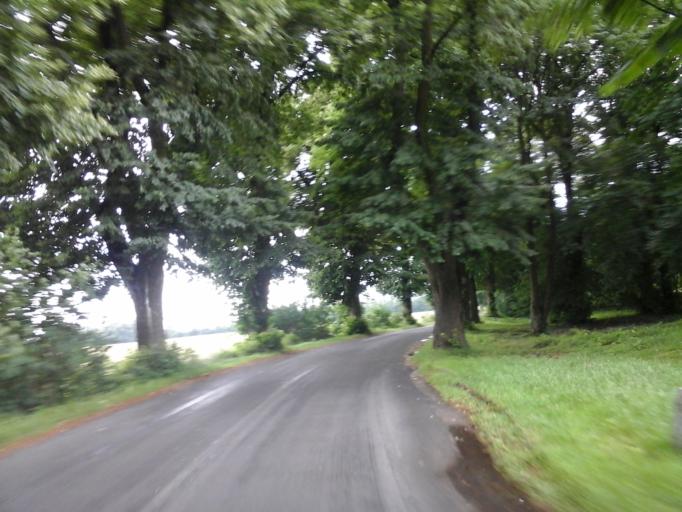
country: PL
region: West Pomeranian Voivodeship
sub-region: Powiat choszczenski
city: Krzecin
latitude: 52.9772
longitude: 15.4944
